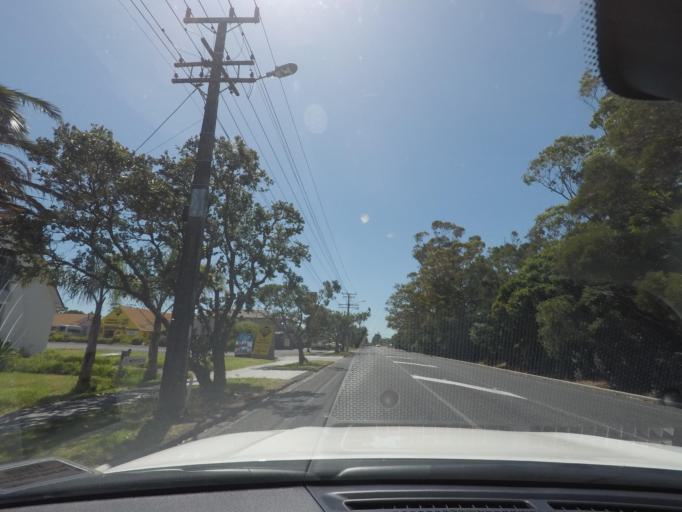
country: NZ
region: Auckland
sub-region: Auckland
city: Parakai
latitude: -36.6598
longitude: 174.4320
